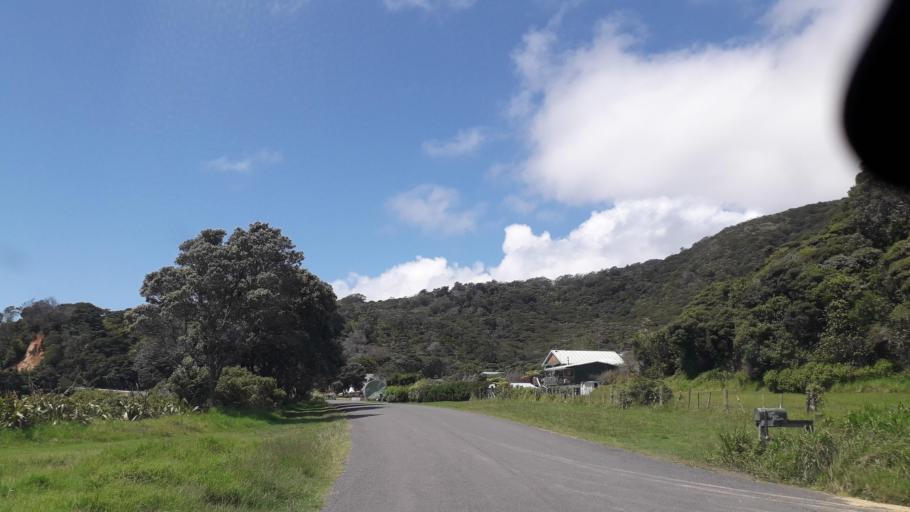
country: NZ
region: Northland
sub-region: Far North District
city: Paihia
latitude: -35.2374
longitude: 174.2586
